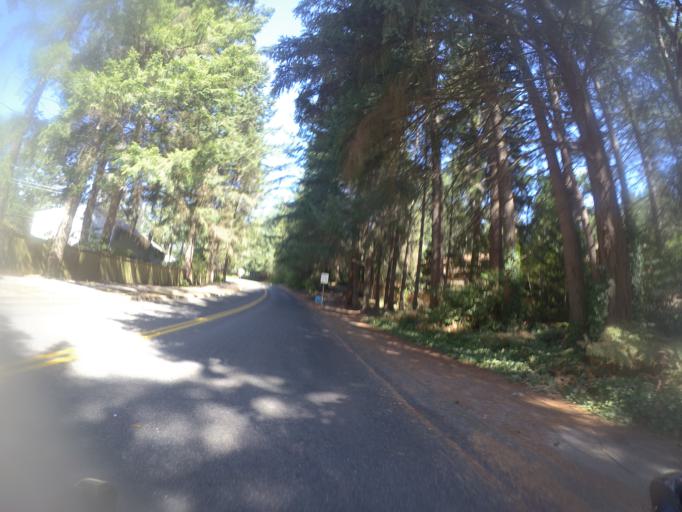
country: US
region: Washington
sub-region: Pierce County
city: University Place
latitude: 47.2129
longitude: -122.5665
